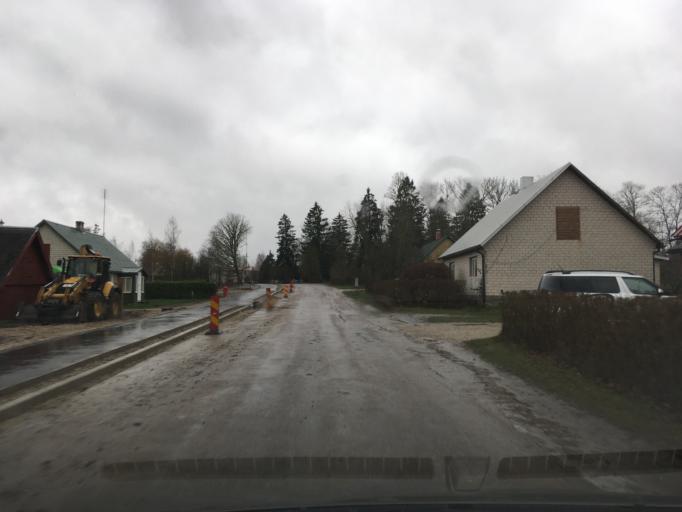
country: EE
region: Laeaene
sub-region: Lihula vald
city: Lihula
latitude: 58.6807
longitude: 23.8234
